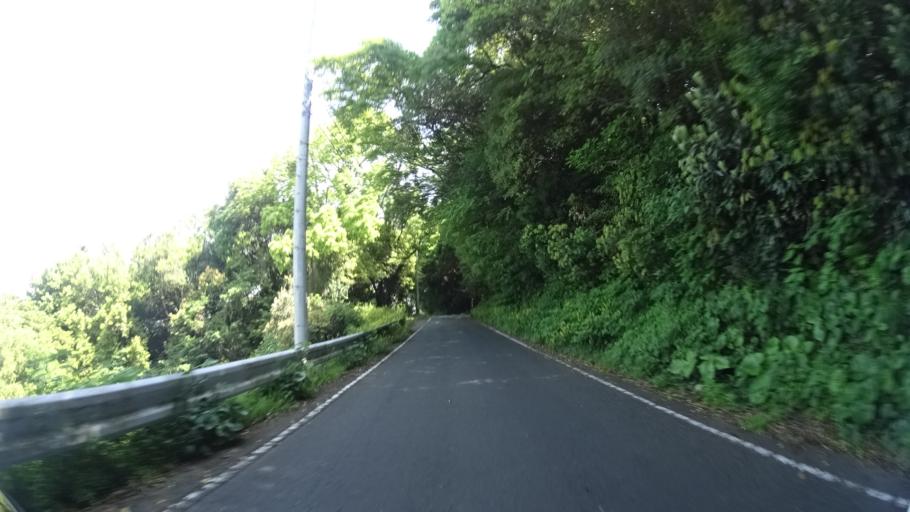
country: JP
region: Ehime
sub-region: Nishiuwa-gun
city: Ikata-cho
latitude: 33.3757
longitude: 132.0603
